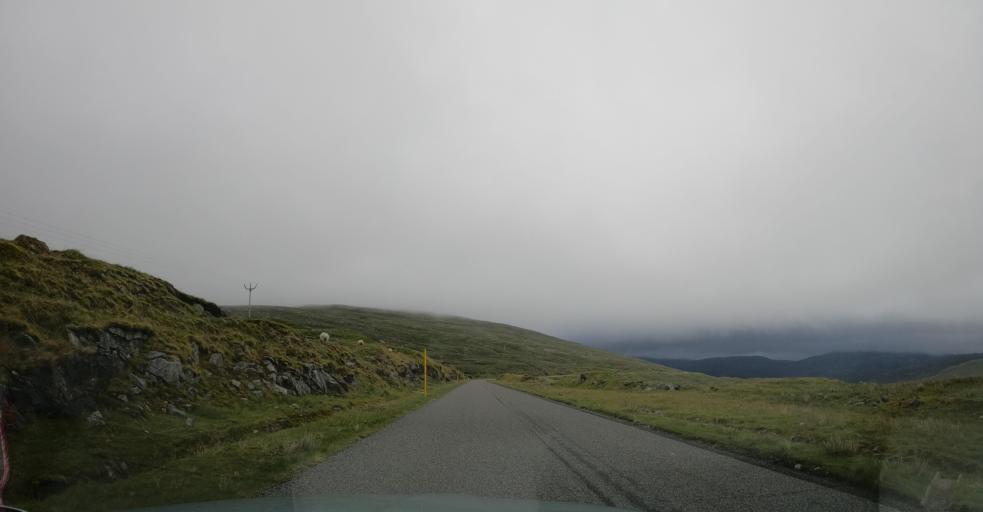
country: GB
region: Scotland
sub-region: Eilean Siar
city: Harris
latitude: 57.9545
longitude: -6.7729
